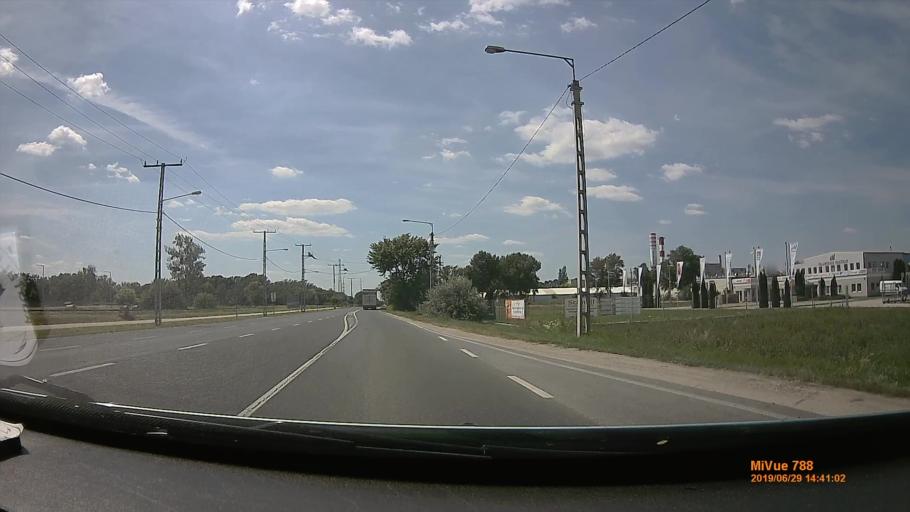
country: HU
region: Komarom-Esztergom
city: Nyergesujfalu
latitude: 47.7572
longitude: 18.5786
